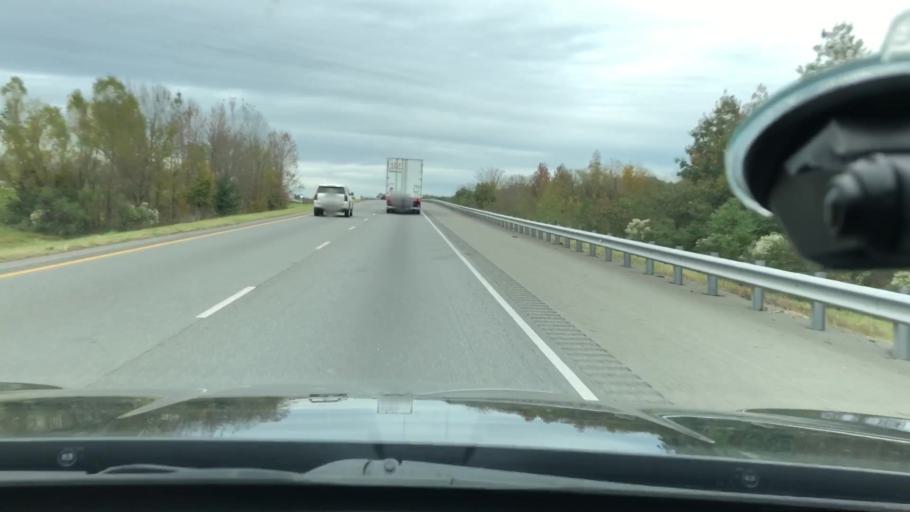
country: US
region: Arkansas
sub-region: Hempstead County
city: Hope
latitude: 33.6735
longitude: -93.6222
